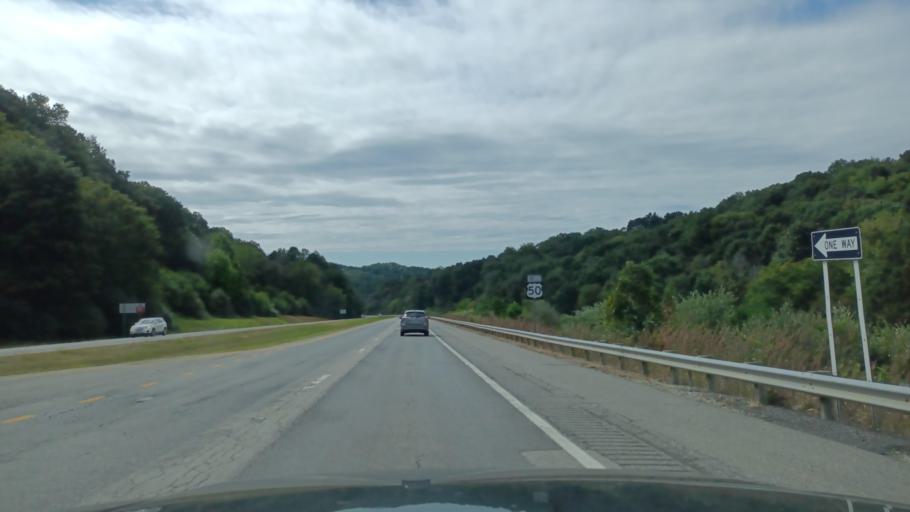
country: US
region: West Virginia
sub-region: Ritchie County
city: Harrisville
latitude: 39.2591
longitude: -81.1680
